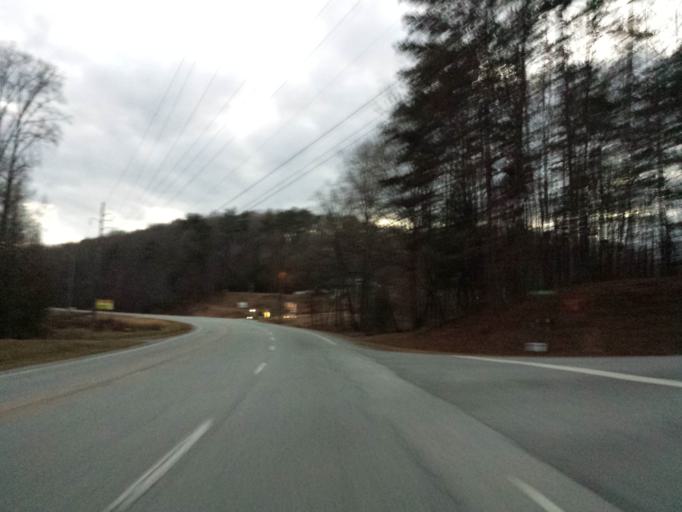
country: US
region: Georgia
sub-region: White County
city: Cleveland
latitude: 34.6580
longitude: -83.7286
